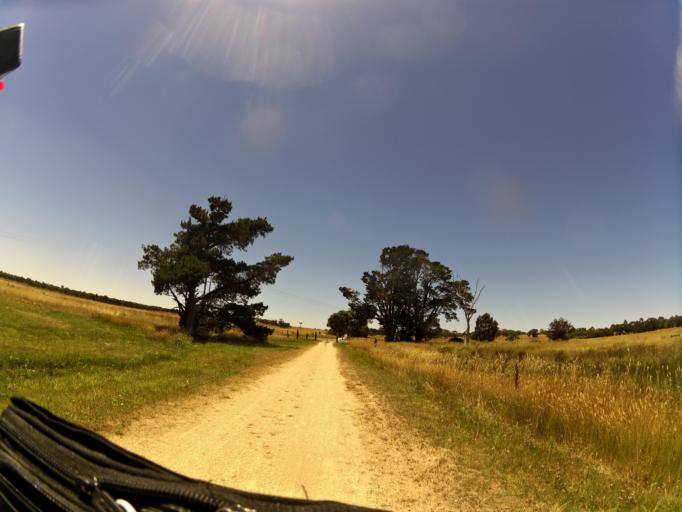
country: AU
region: Victoria
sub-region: Ballarat North
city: Delacombe
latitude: -37.5618
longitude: 143.7372
